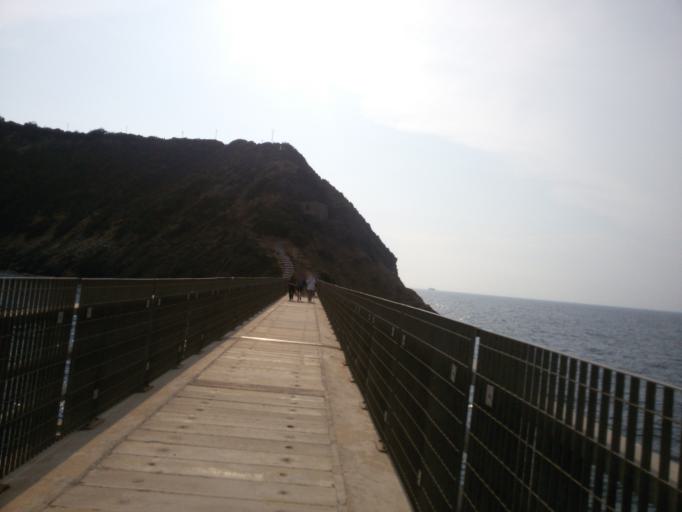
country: IT
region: Campania
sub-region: Provincia di Napoli
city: Procida
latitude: 40.7481
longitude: 13.9988
